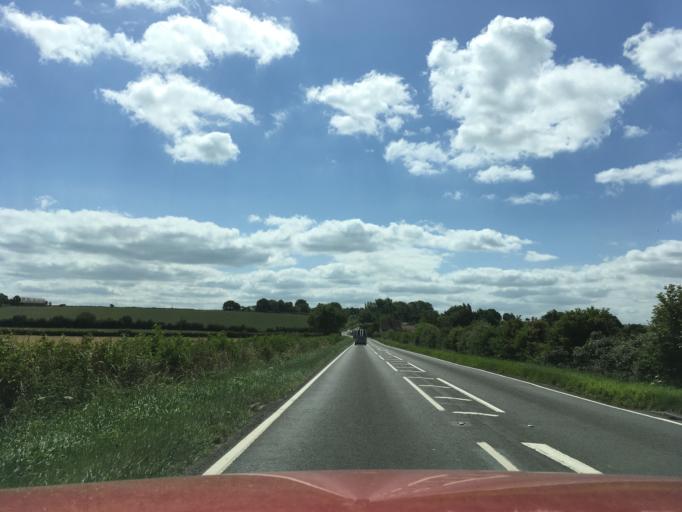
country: GB
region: England
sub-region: Buckinghamshire
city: Winslow
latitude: 51.9013
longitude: -0.8337
